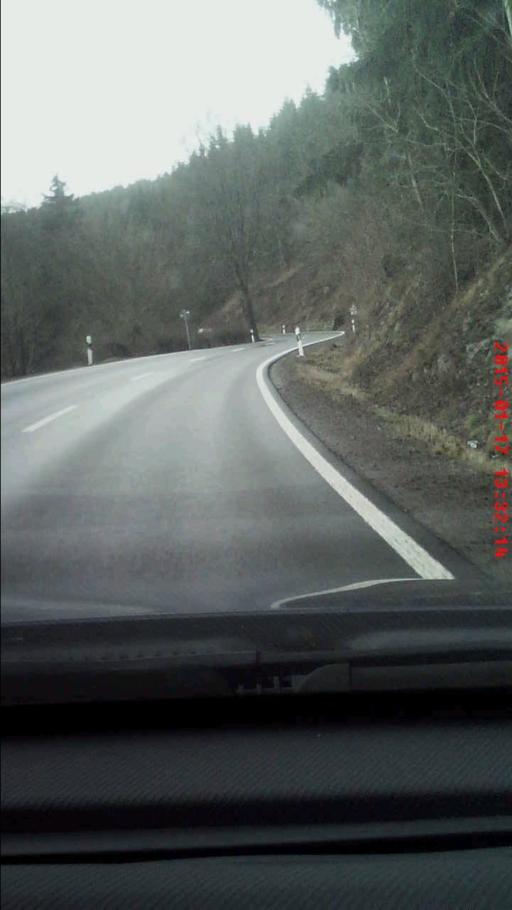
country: DE
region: Thuringia
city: Mohrenbach
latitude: 50.6088
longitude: 10.9841
